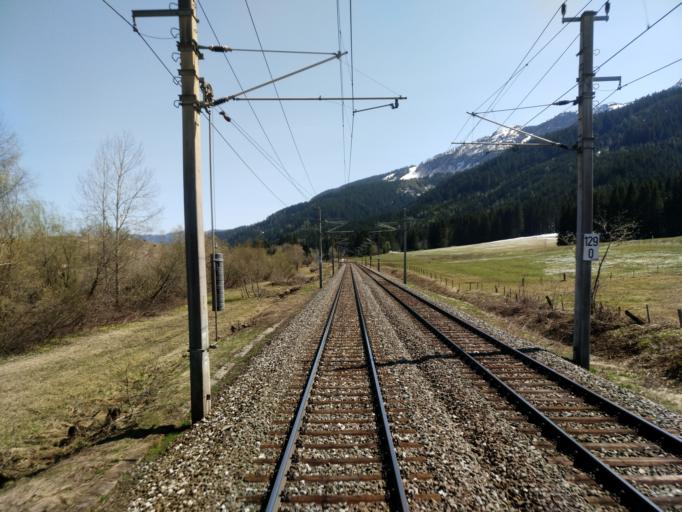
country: AT
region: Tyrol
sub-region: Politischer Bezirk Kitzbuhel
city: Hochfilzen
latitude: 47.4608
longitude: 12.6375
